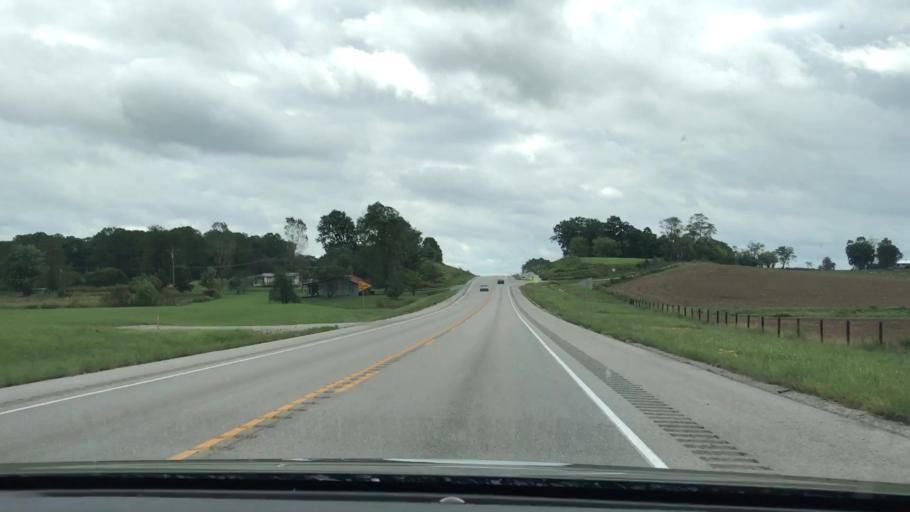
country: US
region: Kentucky
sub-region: Barren County
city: Glasgow
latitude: 36.9516
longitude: -85.8503
